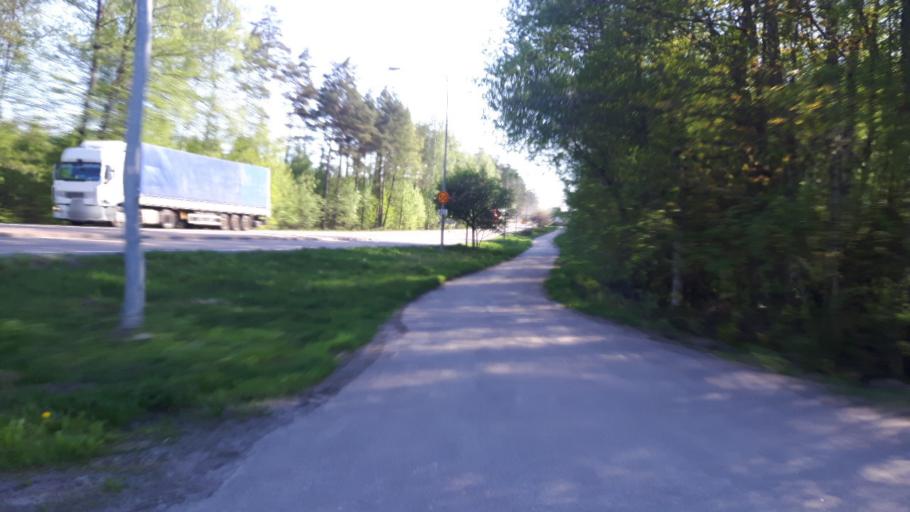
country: FI
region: Kymenlaakso
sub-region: Kotka-Hamina
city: Kotka
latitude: 60.4438
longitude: 26.8886
